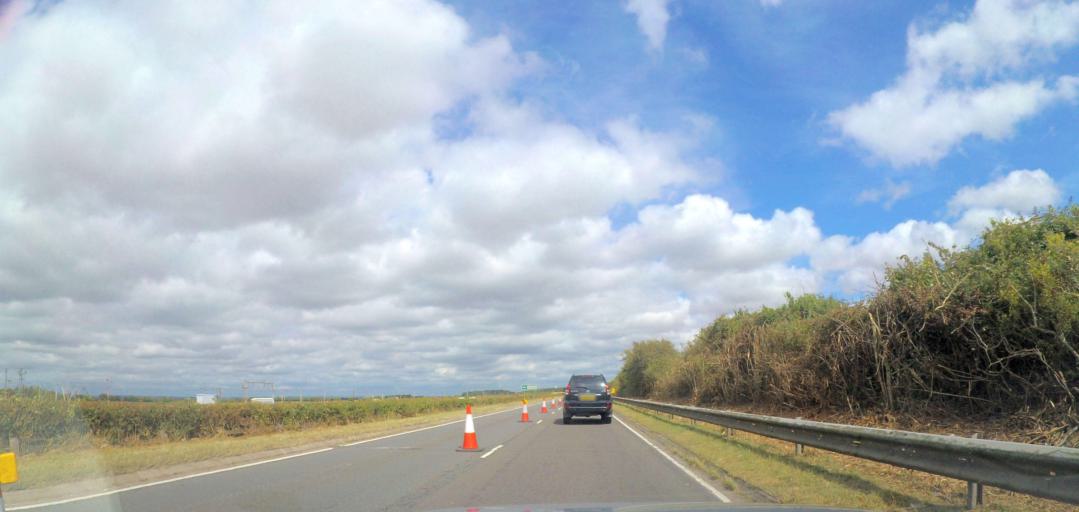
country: GB
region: England
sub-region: Cambridgeshire
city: Bassingbourn
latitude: 52.0423
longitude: -0.0672
